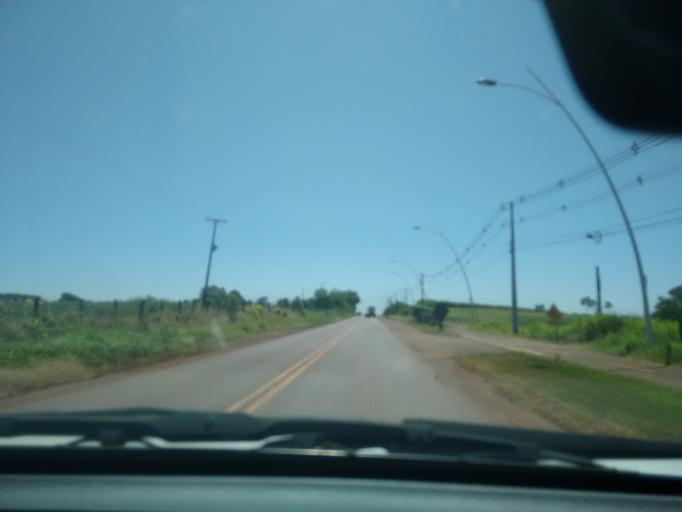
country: BR
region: Parana
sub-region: Marechal Candido Rondon
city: Marechal Candido Rondon
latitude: -24.5573
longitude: -54.0994
